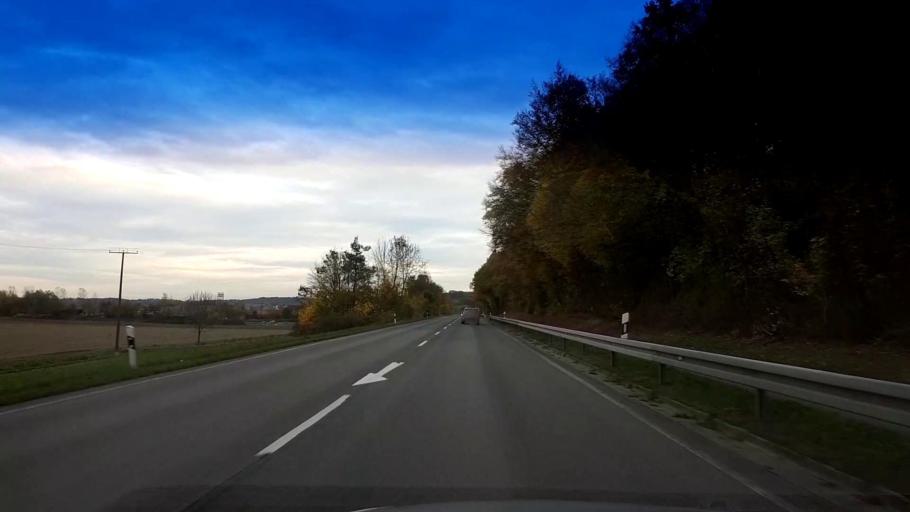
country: DE
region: Bavaria
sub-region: Regierungsbezirk Unterfranken
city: Stettfeld
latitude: 49.9420
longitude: 10.7284
